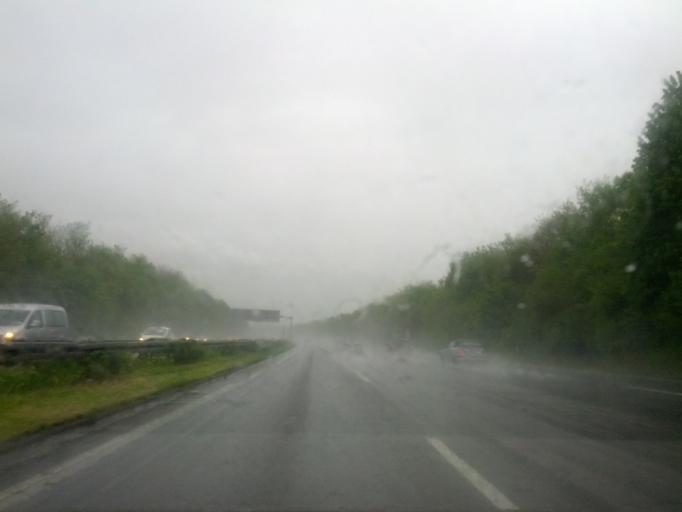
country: DE
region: North Rhine-Westphalia
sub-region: Regierungsbezirk Koln
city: Neustadt/Sued
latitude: 50.8884
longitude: 6.9319
